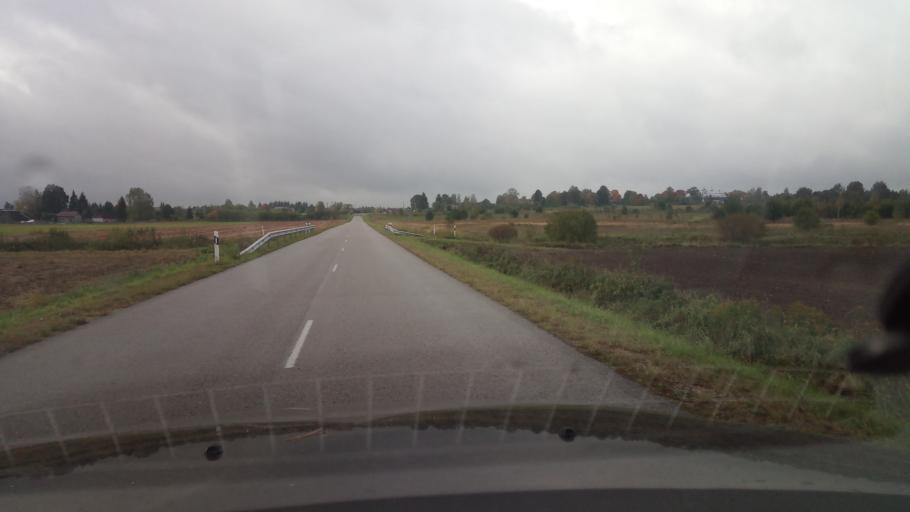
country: LT
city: Skaidiskes
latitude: 54.6166
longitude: 25.5139
